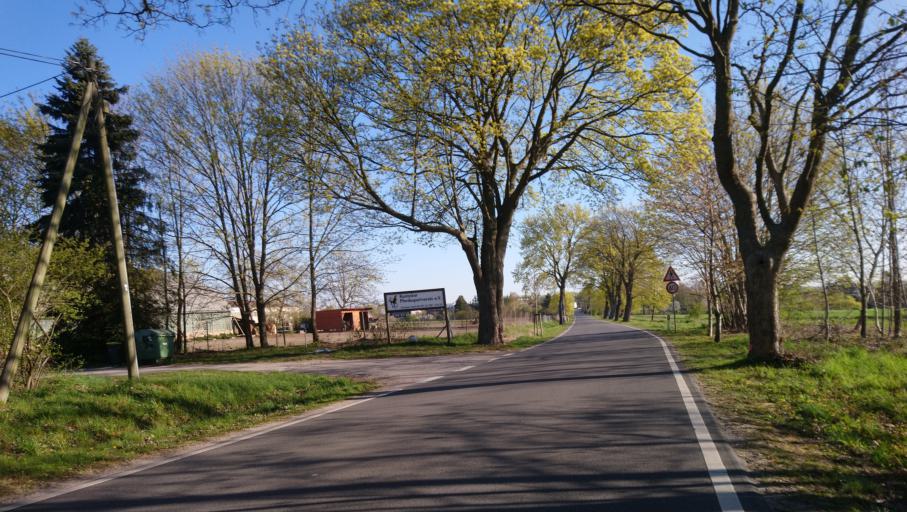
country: DE
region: Mecklenburg-Vorpommern
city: Papendorf
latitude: 54.0593
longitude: 12.1276
